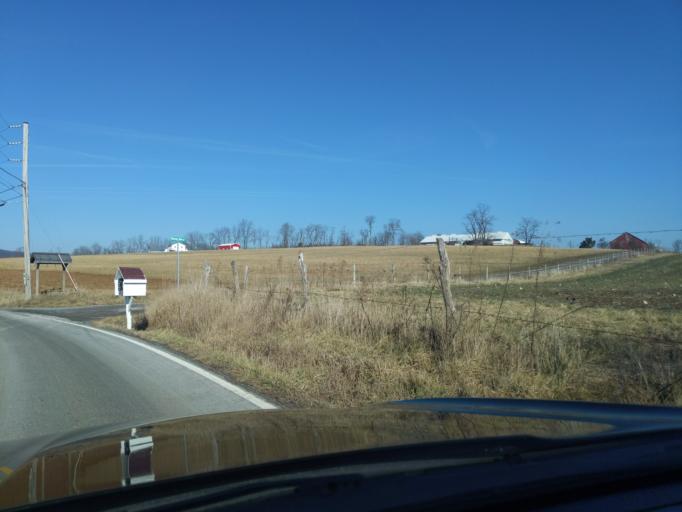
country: US
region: Pennsylvania
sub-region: Blair County
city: Tipton
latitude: 40.5868
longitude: -78.2644
